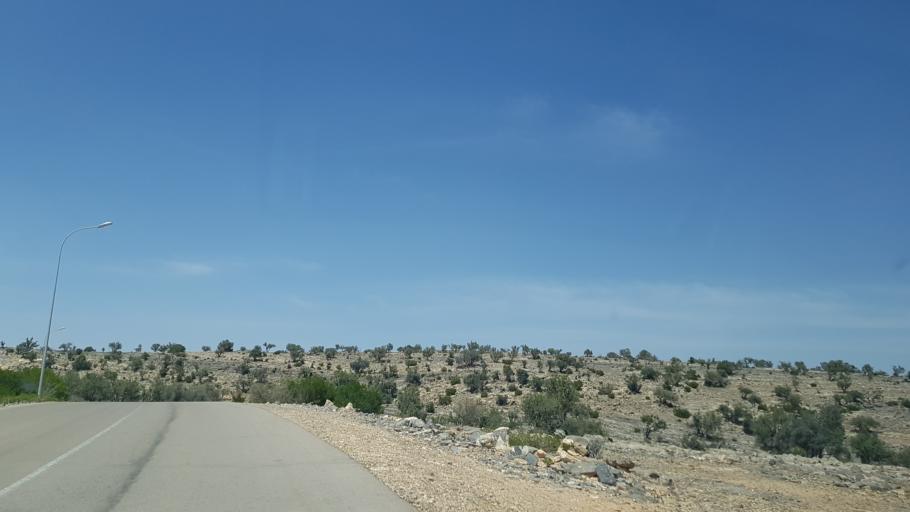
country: OM
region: Muhafazat ad Dakhiliyah
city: Nizwa
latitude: 23.1199
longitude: 57.6033
